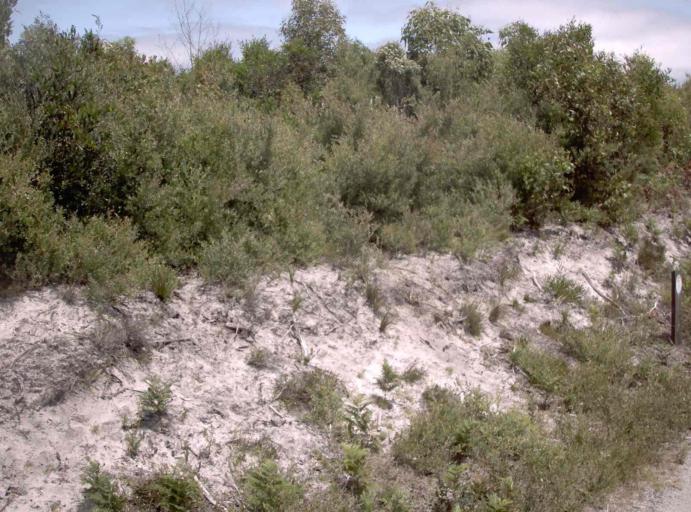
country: AU
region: Victoria
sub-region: Latrobe
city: Morwell
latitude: -39.0306
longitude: 146.3265
